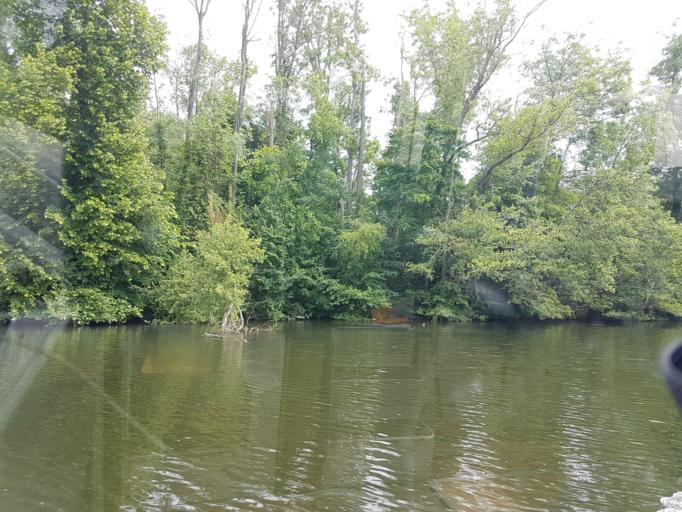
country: FR
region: Bourgogne
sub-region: Departement de l'Yonne
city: Gurgy
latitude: 47.8523
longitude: 3.5599
